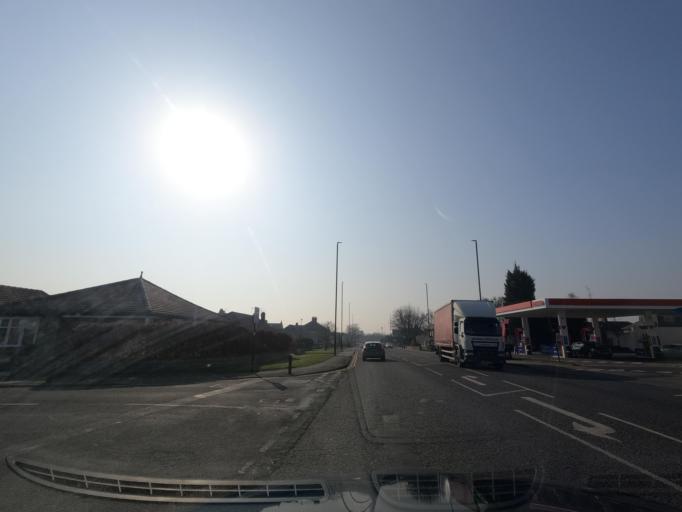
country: GB
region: England
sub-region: Newcastle upon Tyne
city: Gosforth
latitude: 55.0075
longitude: -1.5781
